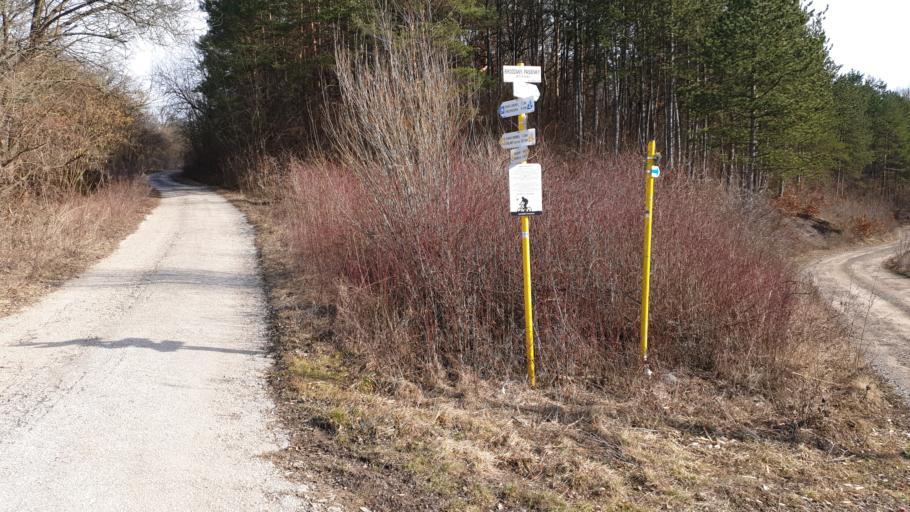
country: SK
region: Nitriansky
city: Partizanske
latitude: 48.6009
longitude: 18.3560
